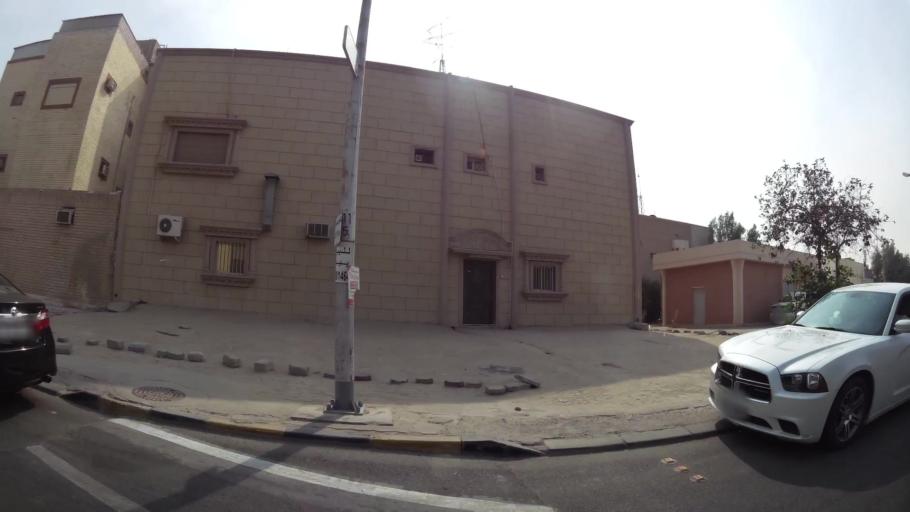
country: KW
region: Al Asimah
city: Ar Rabiyah
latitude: 29.2857
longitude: 47.9435
